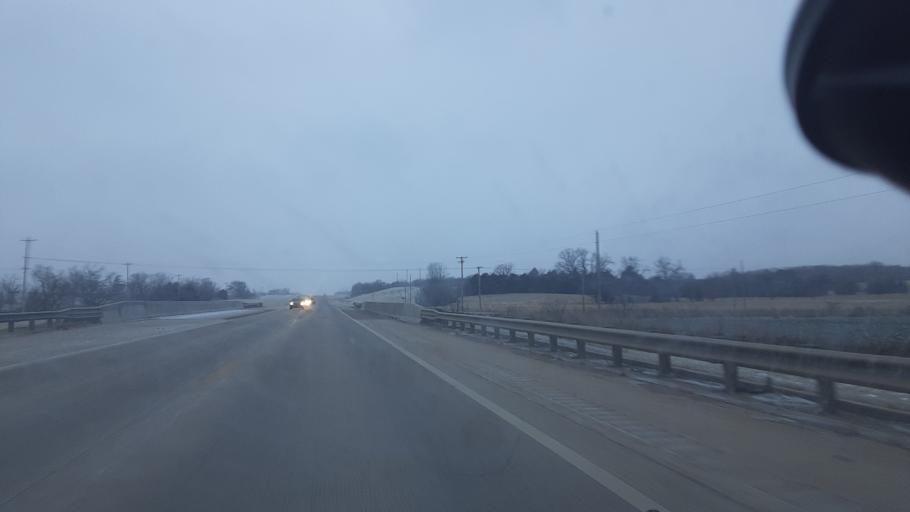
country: US
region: Oklahoma
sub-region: Payne County
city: Perkins
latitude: 35.9859
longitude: -97.1213
